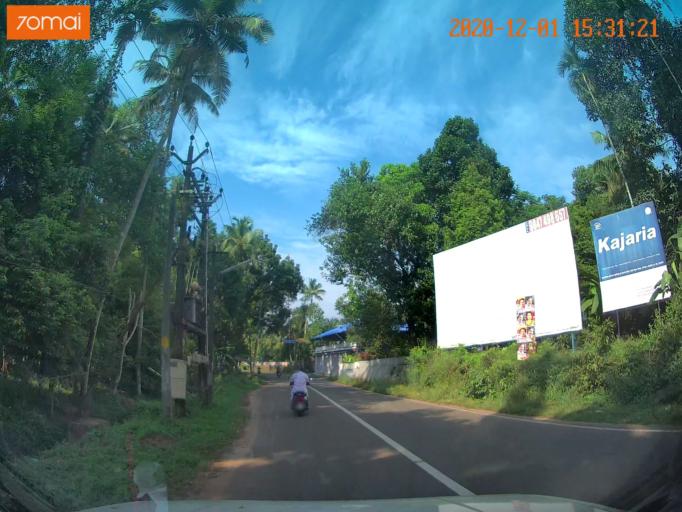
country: IN
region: Kerala
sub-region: Ernakulam
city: Muvattupuzha
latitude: 9.9692
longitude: 76.5693
